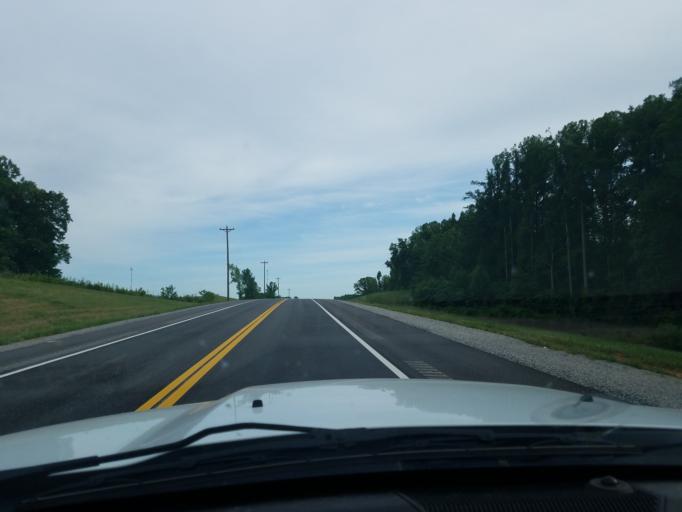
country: US
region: Tennessee
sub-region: Putnam County
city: Cookeville
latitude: 36.1653
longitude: -85.5627
